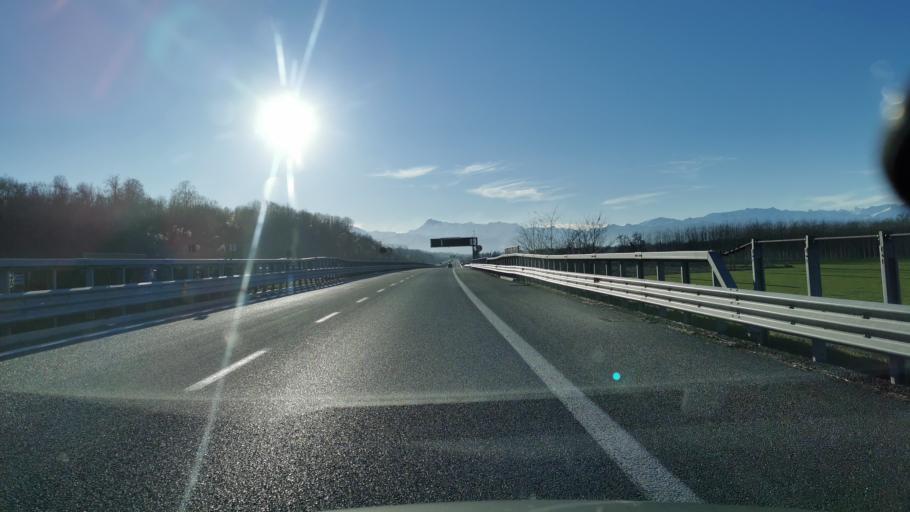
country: IT
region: Piedmont
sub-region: Provincia di Cuneo
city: Castelletto Stura
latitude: 44.4430
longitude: 7.6313
